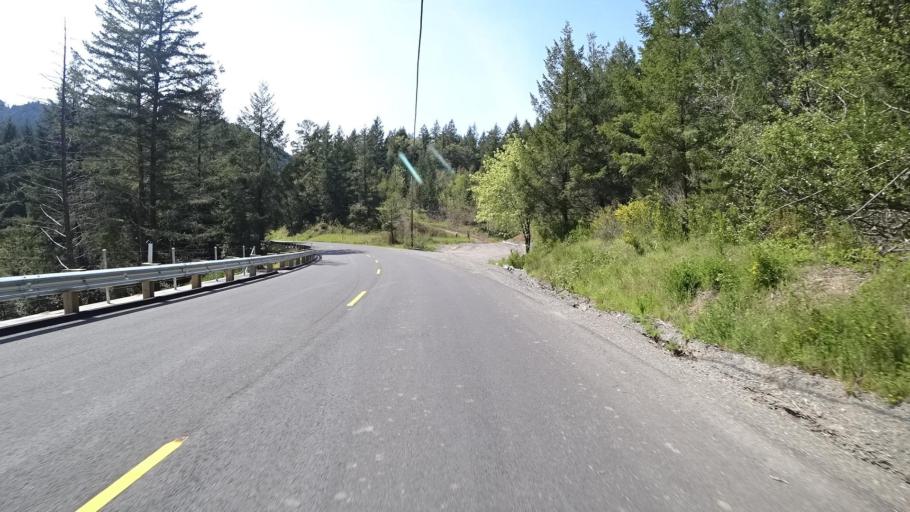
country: US
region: California
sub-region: Humboldt County
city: Rio Dell
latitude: 40.4423
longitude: -123.7876
